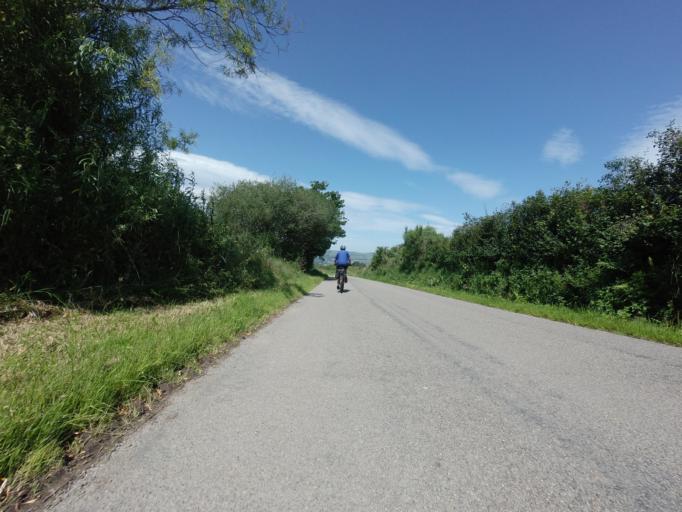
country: GB
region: Scotland
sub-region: Highland
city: Conon Bridge
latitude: 57.5562
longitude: -4.4088
